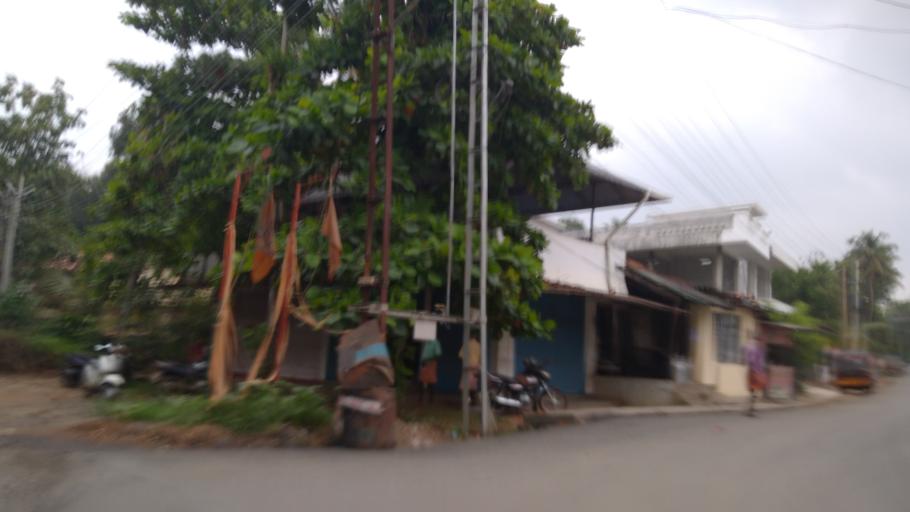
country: IN
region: Kerala
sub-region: Ernakulam
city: Perumbavoor
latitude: 10.0634
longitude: 76.5042
